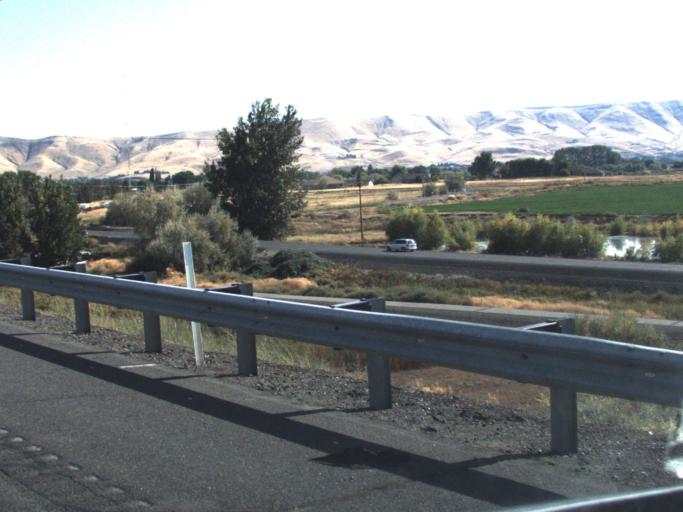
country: US
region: Washington
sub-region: Benton County
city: Prosser
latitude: 46.2378
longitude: -119.8177
